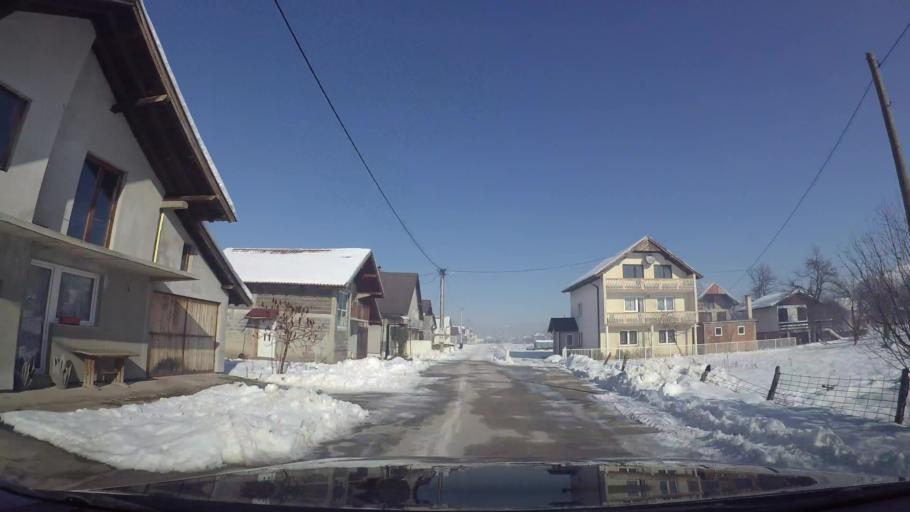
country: BA
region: Federation of Bosnia and Herzegovina
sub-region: Kanton Sarajevo
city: Sarajevo
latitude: 43.7921
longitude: 18.3396
